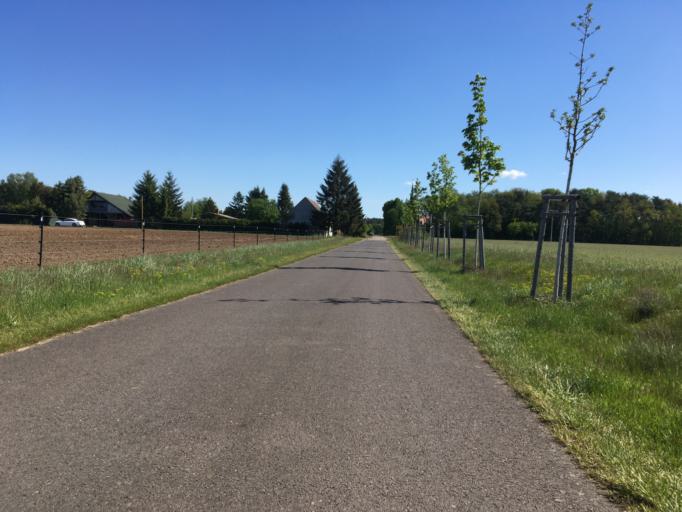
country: DE
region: Brandenburg
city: Liebenwalde
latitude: 52.9625
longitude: 13.4333
